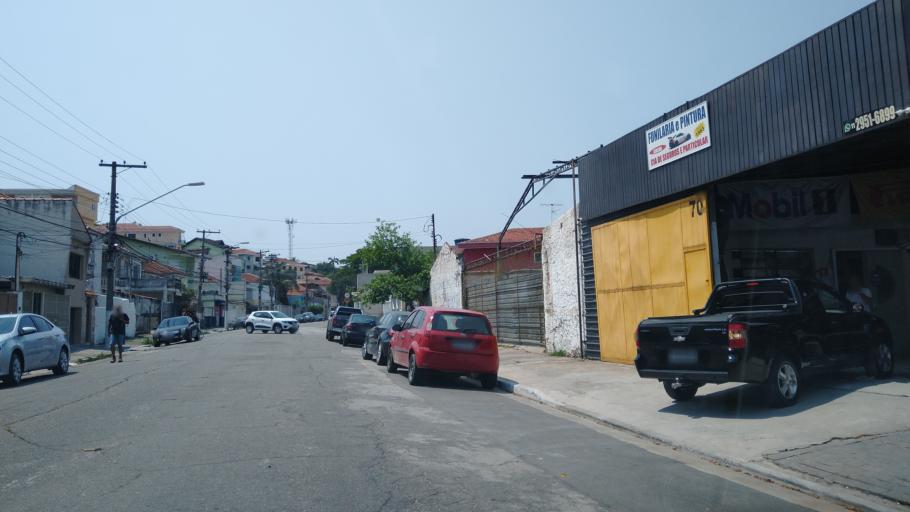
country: BR
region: Sao Paulo
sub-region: Sao Paulo
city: Sao Paulo
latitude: -23.4961
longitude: -46.6098
